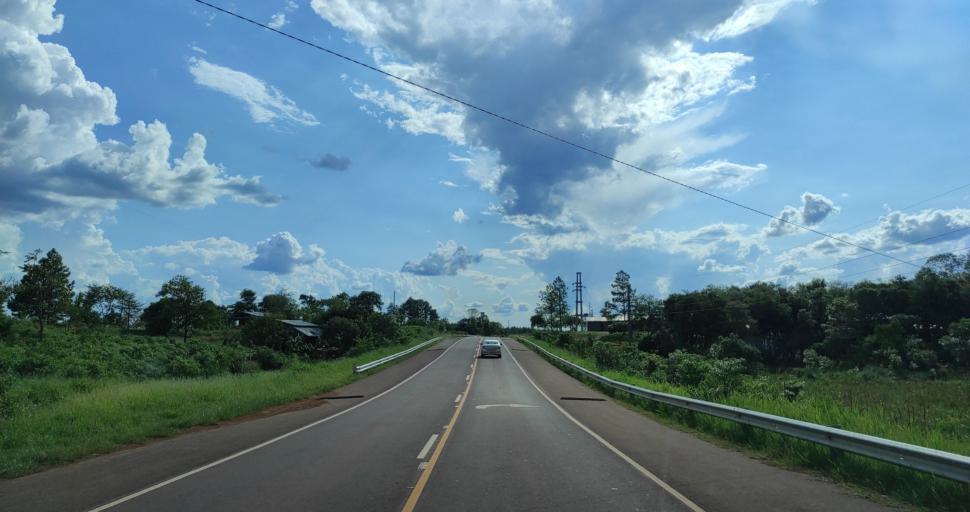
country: AR
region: Misiones
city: Bernardo de Irigoyen
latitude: -26.2985
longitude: -53.7989
